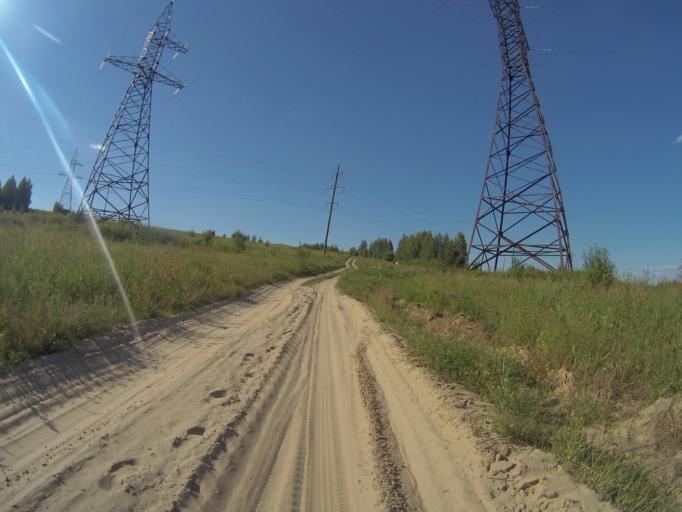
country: RU
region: Vladimir
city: Raduzhnyy
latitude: 55.9962
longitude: 40.3718
